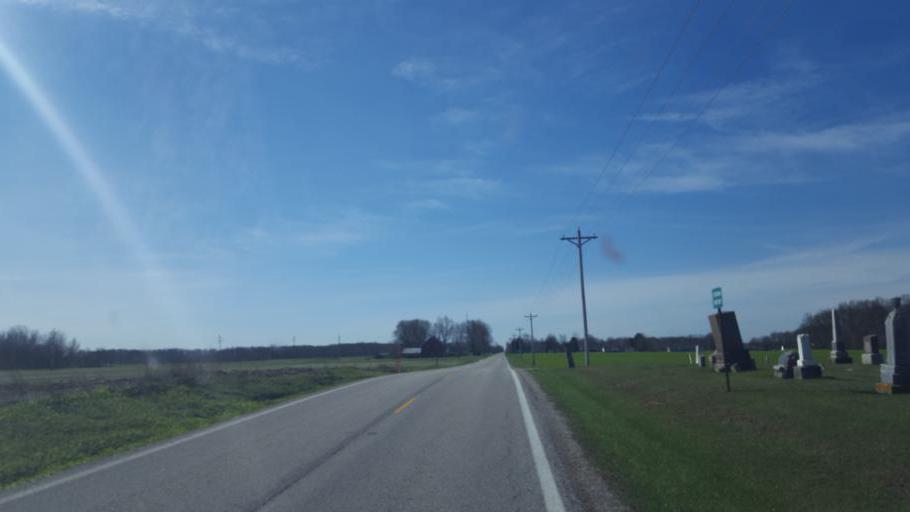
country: US
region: Ohio
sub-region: Morrow County
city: Cardington
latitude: 40.5639
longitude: -82.9623
